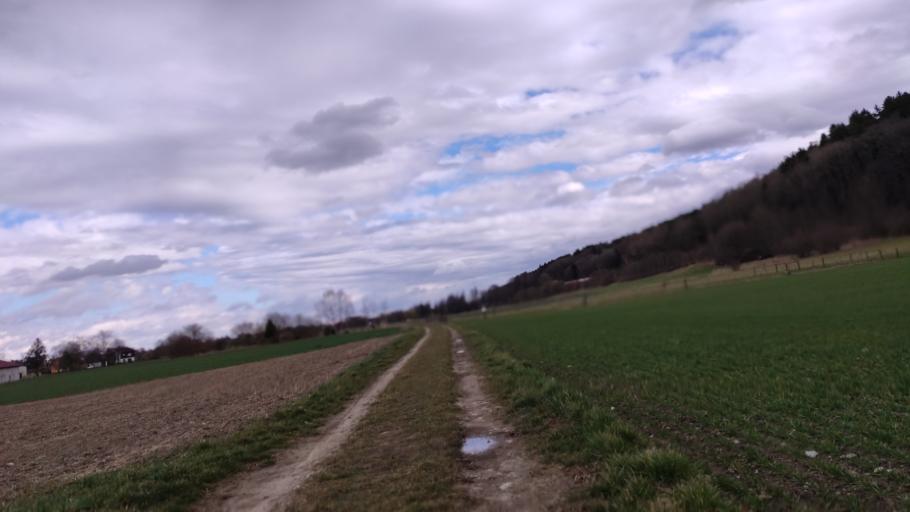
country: DE
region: Bavaria
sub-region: Upper Bavaria
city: Emmering
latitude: 48.1756
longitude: 11.2817
